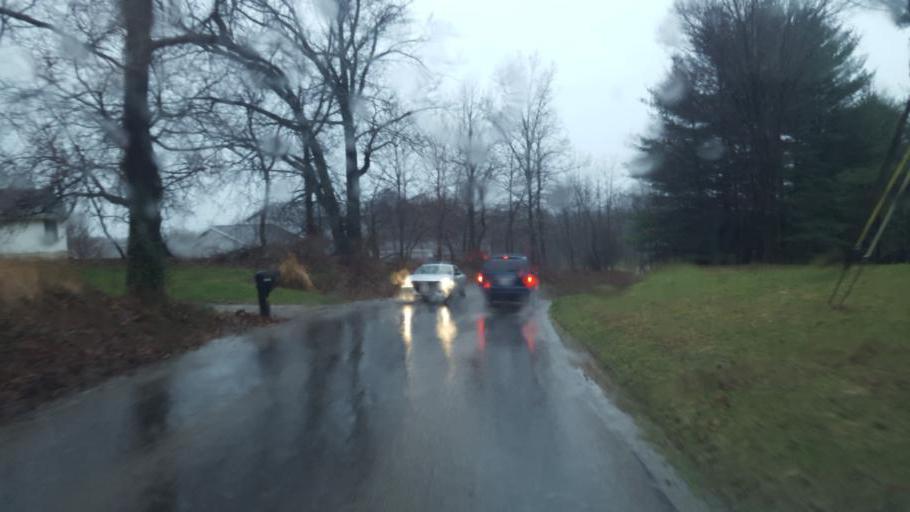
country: US
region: Ohio
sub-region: Knox County
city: Mount Vernon
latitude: 40.4196
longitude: -82.4843
